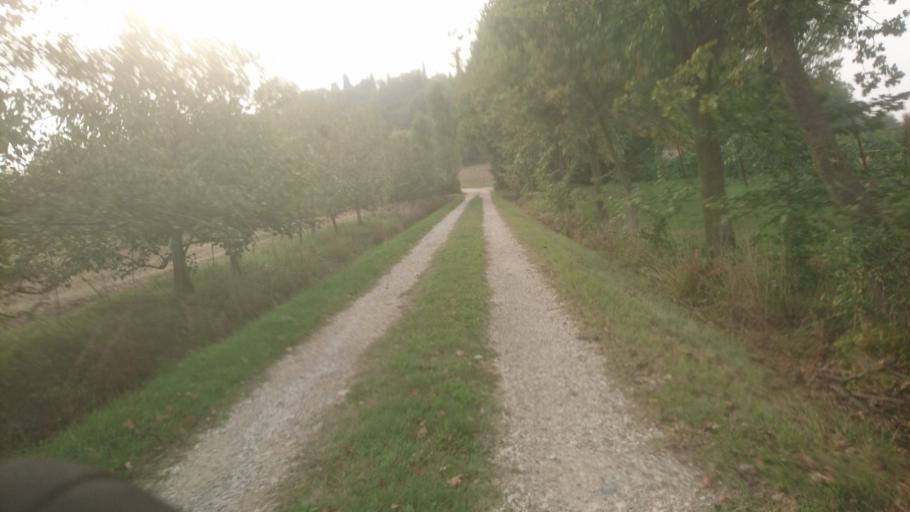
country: IT
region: Veneto
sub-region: Provincia di Vicenza
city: Montegalda
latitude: 45.4446
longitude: 11.6837
